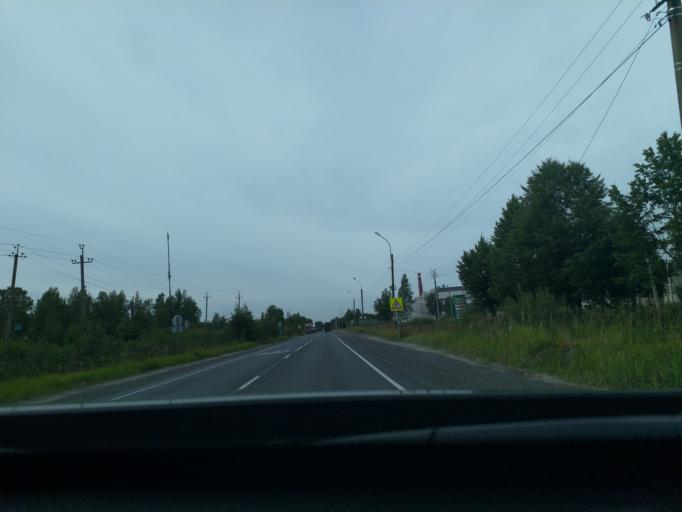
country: RU
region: Leningrad
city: Nikol'skoye
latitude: 59.7251
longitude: 30.7780
